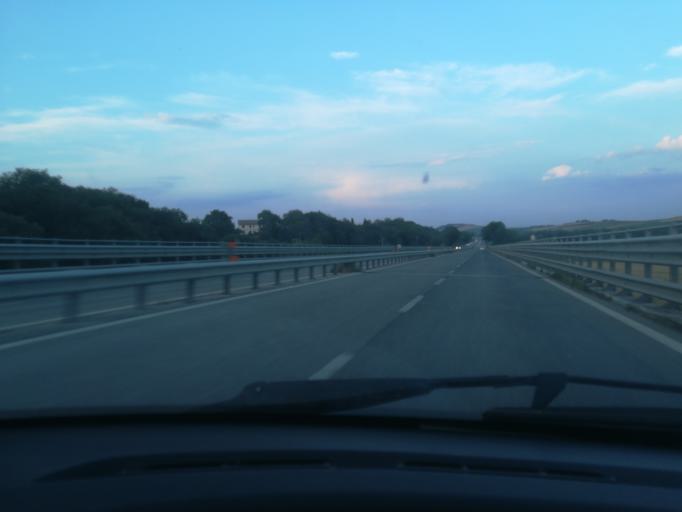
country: IT
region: The Marches
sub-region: Provincia di Macerata
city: Pollenza
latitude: 43.2326
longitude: 13.3579
